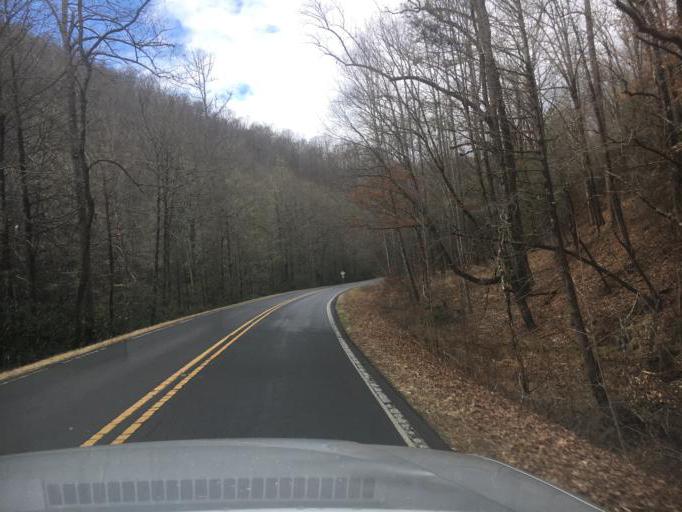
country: US
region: North Carolina
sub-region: Transylvania County
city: Brevard
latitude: 35.2804
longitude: -82.7537
